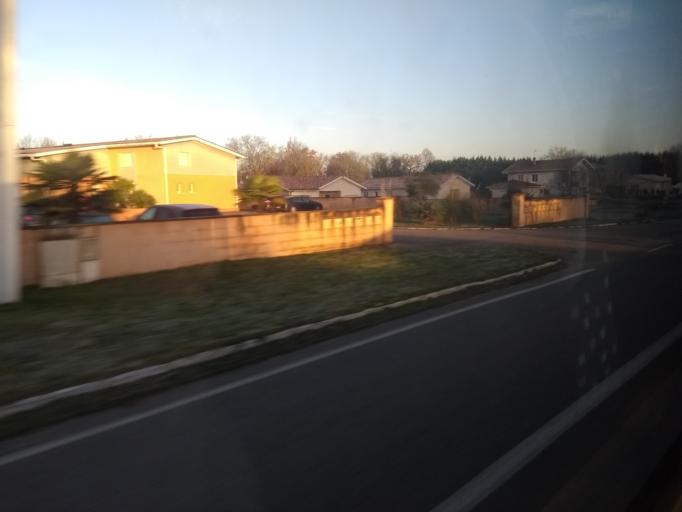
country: FR
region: Aquitaine
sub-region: Departement de la Gironde
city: Le Barp
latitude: 44.6120
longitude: -0.7665
